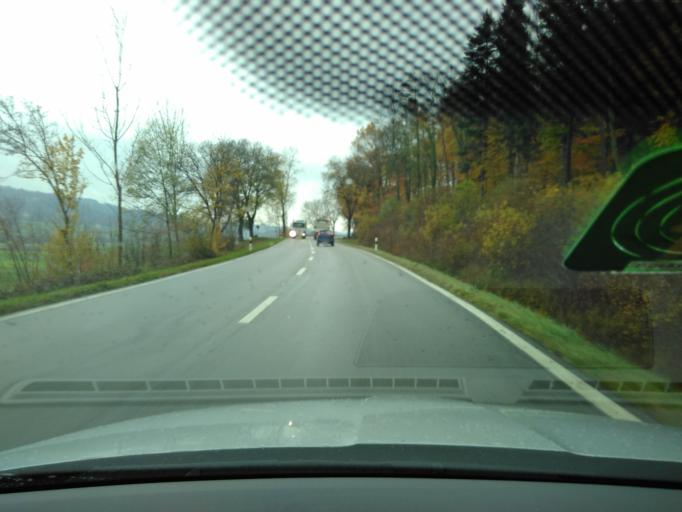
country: CH
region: Aargau
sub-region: Bezirk Zofingen
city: Kirchleerau
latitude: 47.2592
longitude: 8.0648
